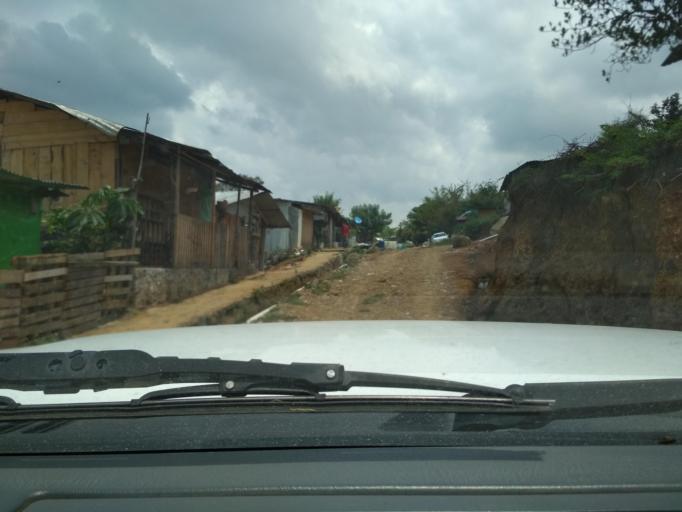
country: MX
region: Veracruz
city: Cordoba
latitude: 18.8871
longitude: -96.9176
